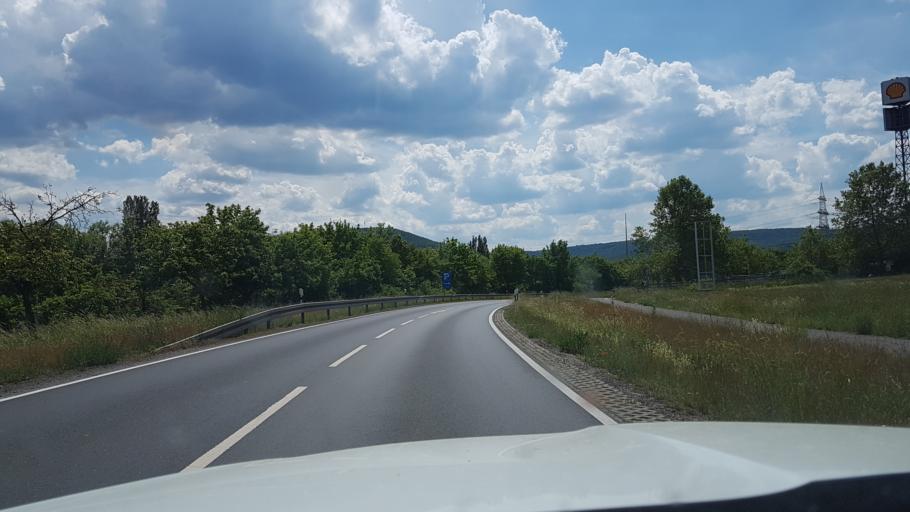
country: DE
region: Bavaria
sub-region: Regierungsbezirk Unterfranken
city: Knetzgau
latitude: 49.9834
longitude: 10.5557
